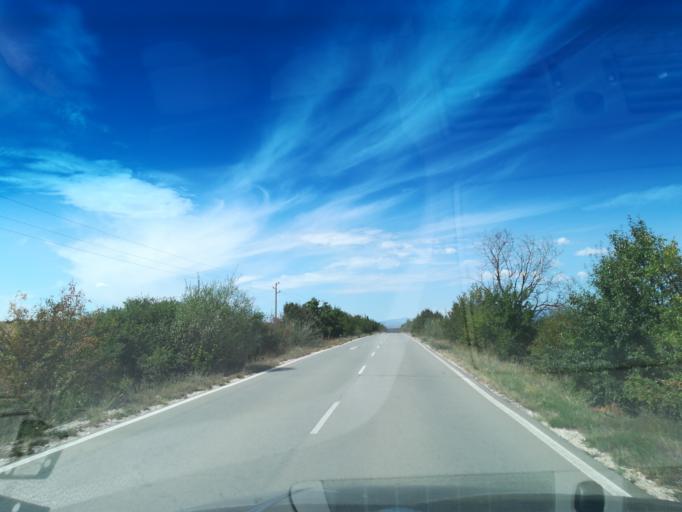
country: BG
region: Plovdiv
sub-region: Obshtina Suedinenie
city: Suedinenie
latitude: 42.4015
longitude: 24.5354
